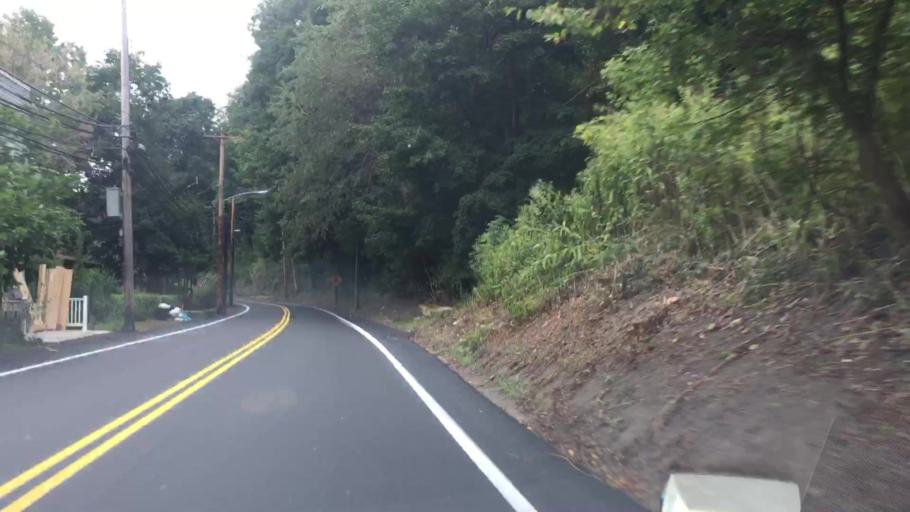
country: US
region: Pennsylvania
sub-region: Allegheny County
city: Carnegie
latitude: 40.4115
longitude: -80.0937
